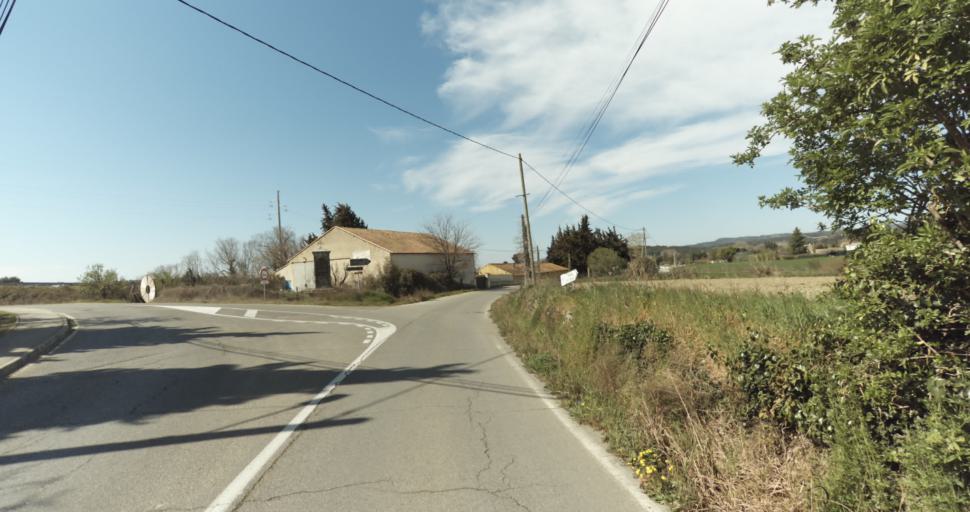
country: FR
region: Provence-Alpes-Cote d'Azur
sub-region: Departement des Bouches-du-Rhone
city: Lambesc
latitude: 43.6510
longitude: 5.2518
